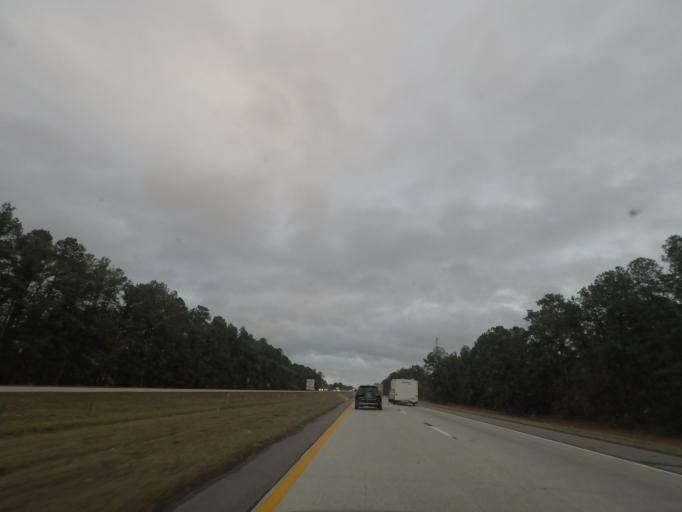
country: US
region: South Carolina
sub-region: Dorchester County
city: Saint George
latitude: 33.2621
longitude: -80.5735
